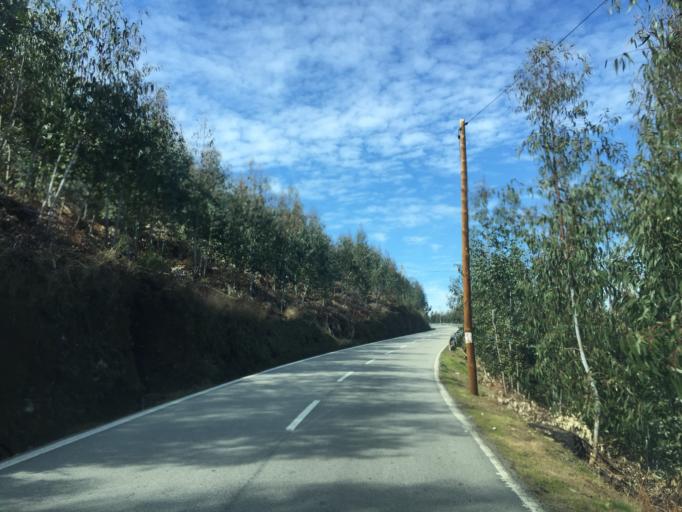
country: PT
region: Aveiro
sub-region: Arouca
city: Arouca
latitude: 40.9590
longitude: -8.2022
